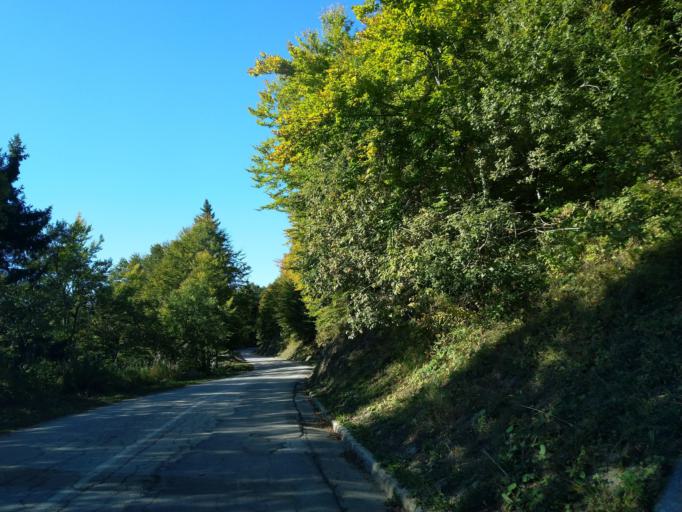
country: RS
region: Central Serbia
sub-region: Moravicki Okrug
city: Ivanjica
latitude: 43.4178
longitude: 20.2661
